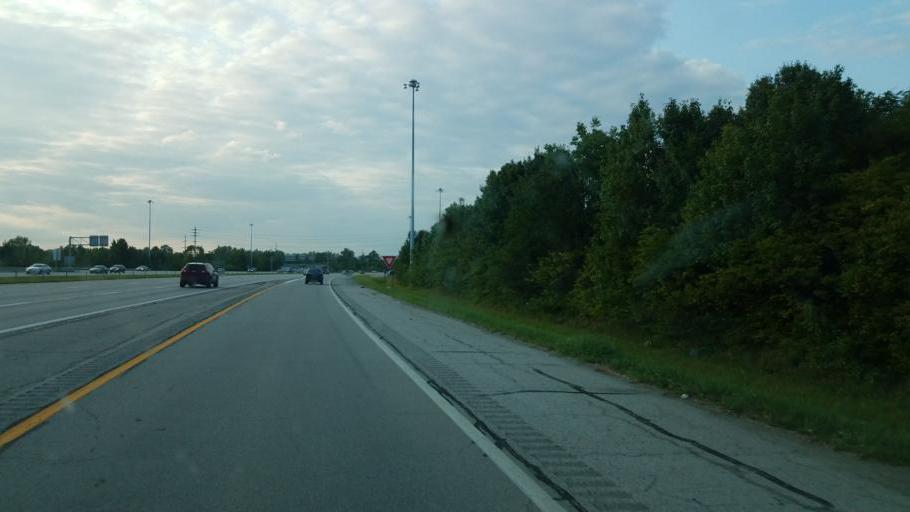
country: US
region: Ohio
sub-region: Franklin County
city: Whitehall
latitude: 39.9811
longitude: -82.8547
